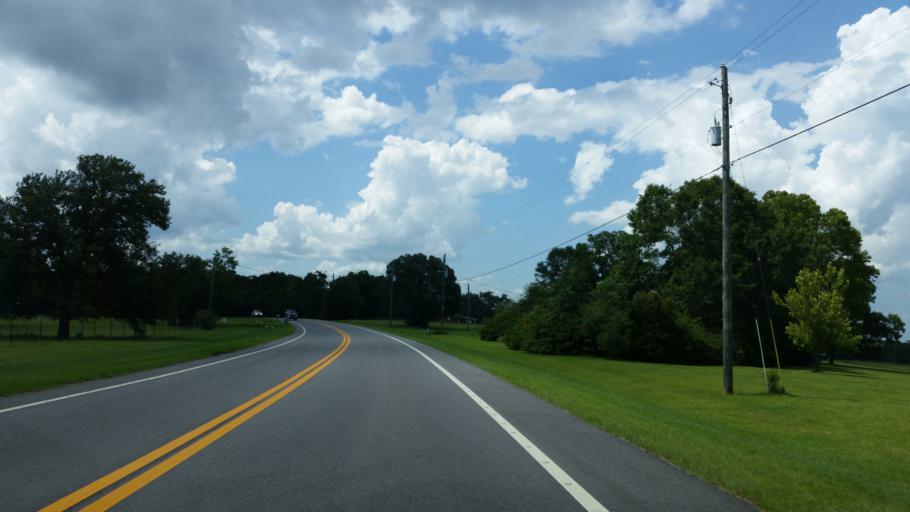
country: US
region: Florida
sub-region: Escambia County
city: Cantonment
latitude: 30.6317
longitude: -87.3777
